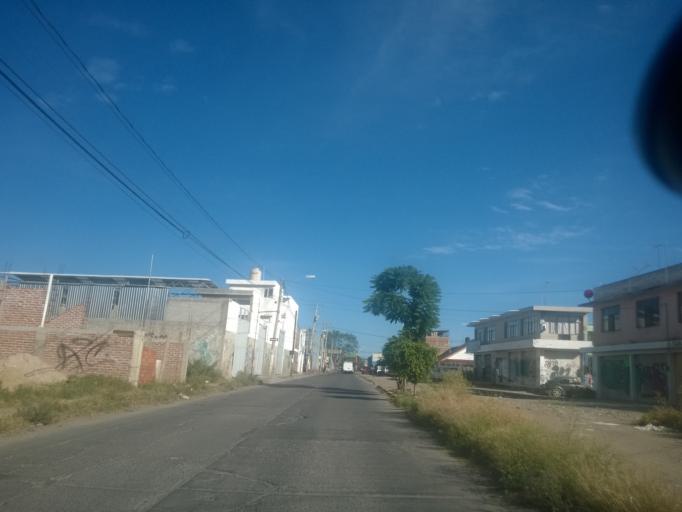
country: MX
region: Guanajuato
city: Leon
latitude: 21.1249
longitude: -101.6501
